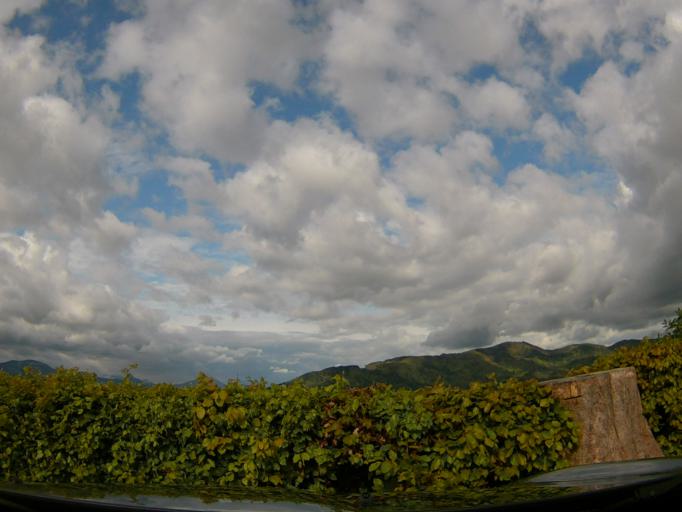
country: AT
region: Upper Austria
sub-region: Politischer Bezirk Vocklabruck
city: Mondsee
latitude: 47.8679
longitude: 13.3520
